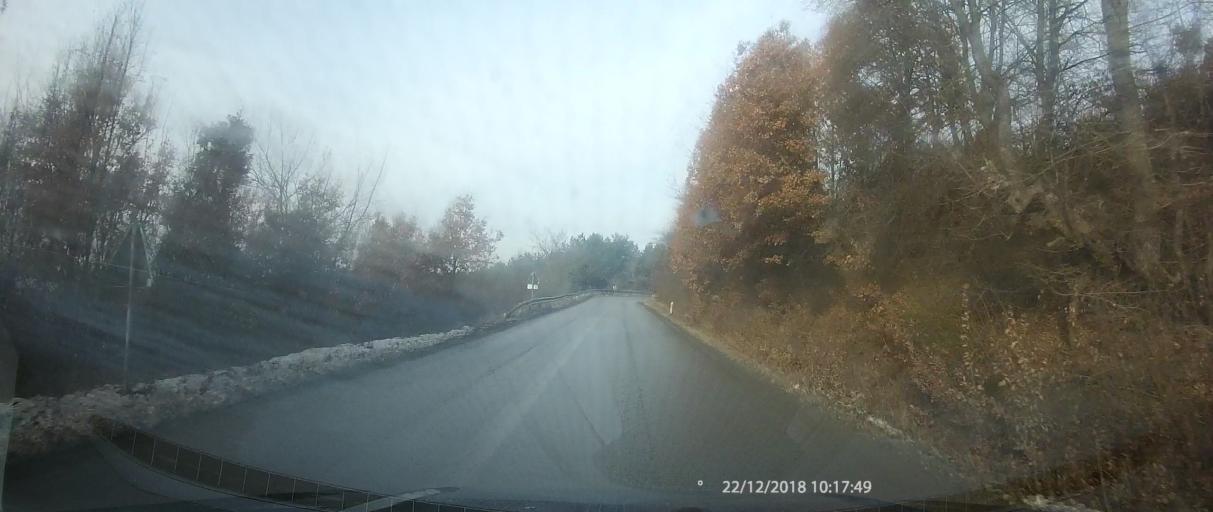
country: MK
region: Kriva Palanka
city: Kriva Palanka
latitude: 42.1836
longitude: 22.2800
